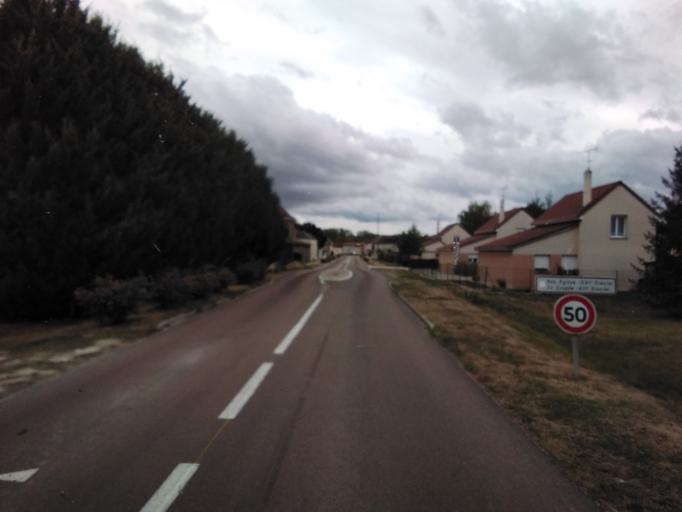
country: FR
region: Champagne-Ardenne
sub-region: Departement de l'Aube
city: Brienne-le-Chateau
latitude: 48.4639
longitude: 4.5020
